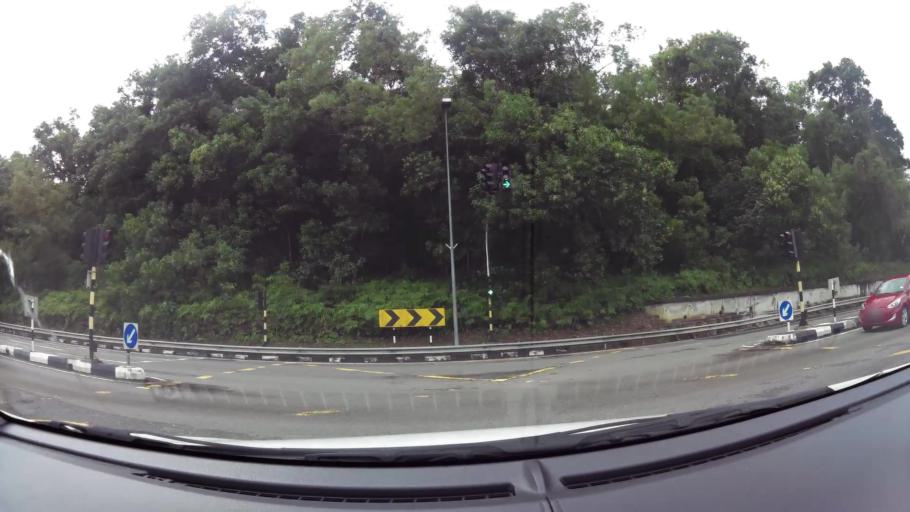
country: BN
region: Brunei and Muara
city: Bandar Seri Begawan
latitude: 4.9055
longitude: 114.9406
